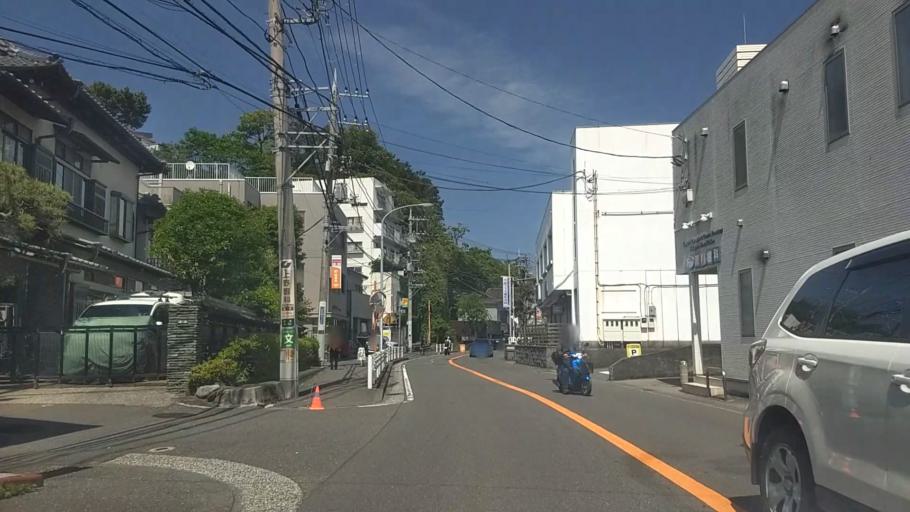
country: JP
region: Kanagawa
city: Zushi
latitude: 35.3222
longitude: 139.6097
